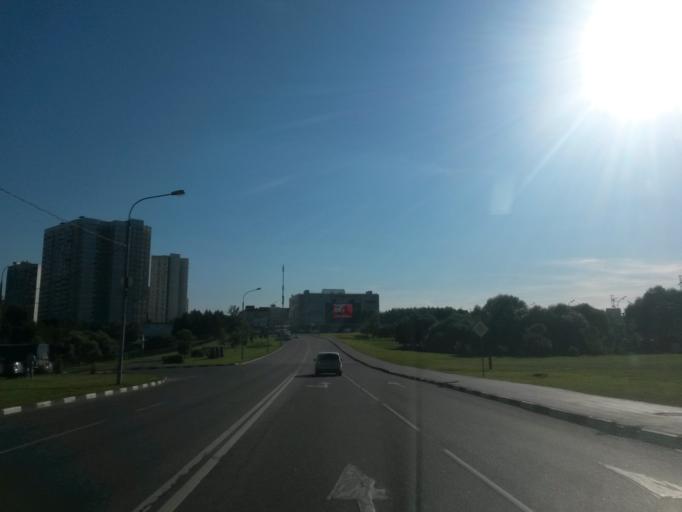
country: RU
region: Moscow
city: Chertanovo Yuzhnoye
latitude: 55.5768
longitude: 37.5691
